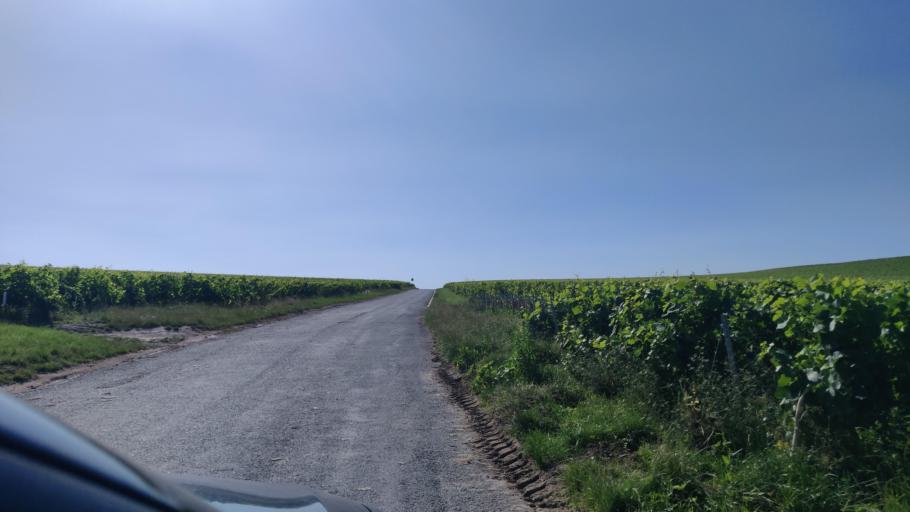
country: FR
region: Champagne-Ardenne
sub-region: Departement de la Marne
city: Tours-sur-Marne
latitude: 49.0893
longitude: 4.1252
